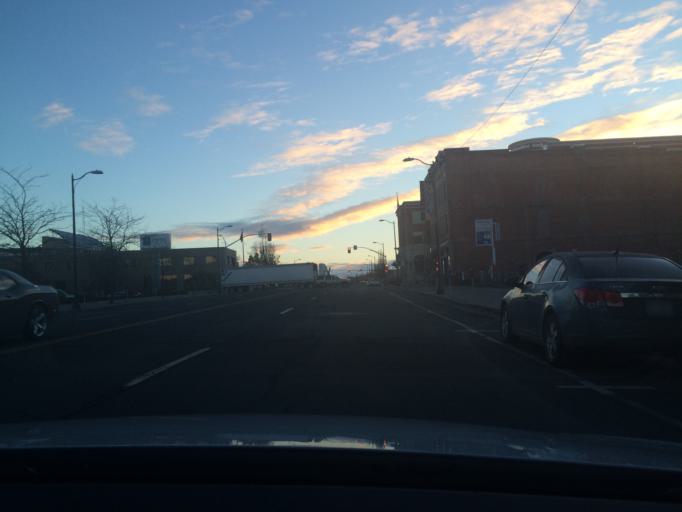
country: US
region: Washington
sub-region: Spokane County
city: Spokane
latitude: 47.6580
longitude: -117.4145
